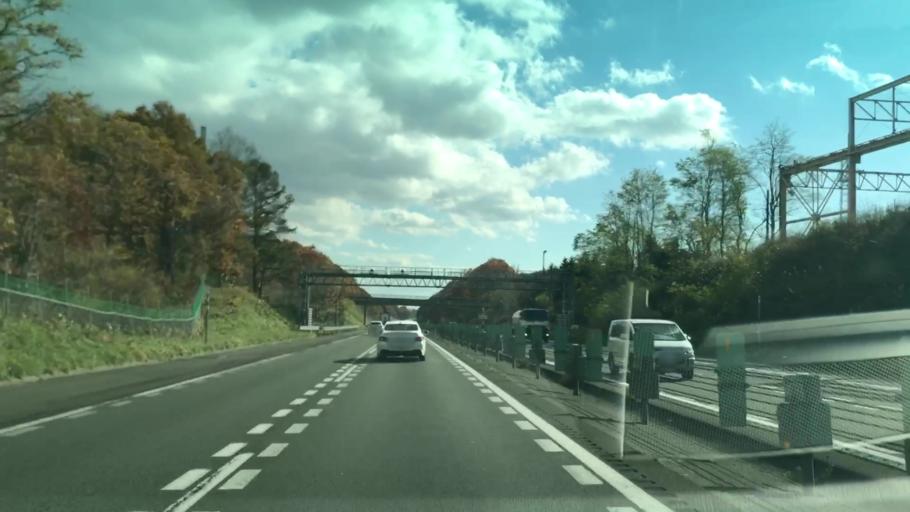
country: JP
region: Hokkaido
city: Kitahiroshima
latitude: 42.9339
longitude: 141.5282
